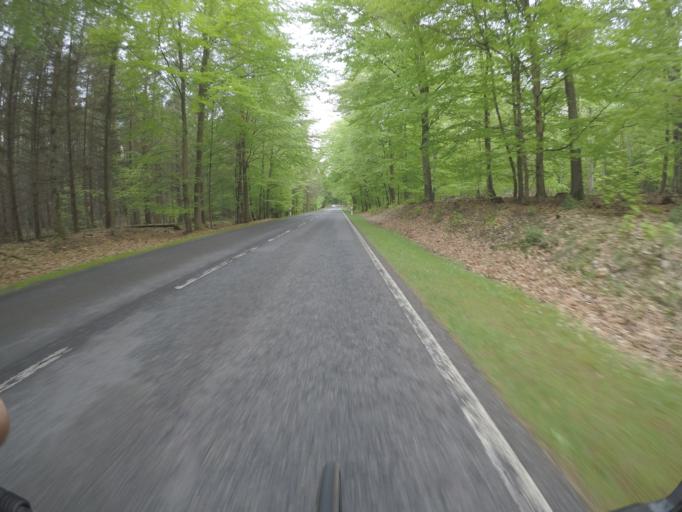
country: DE
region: Brandenburg
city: Joachimsthal
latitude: 52.9364
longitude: 13.7362
